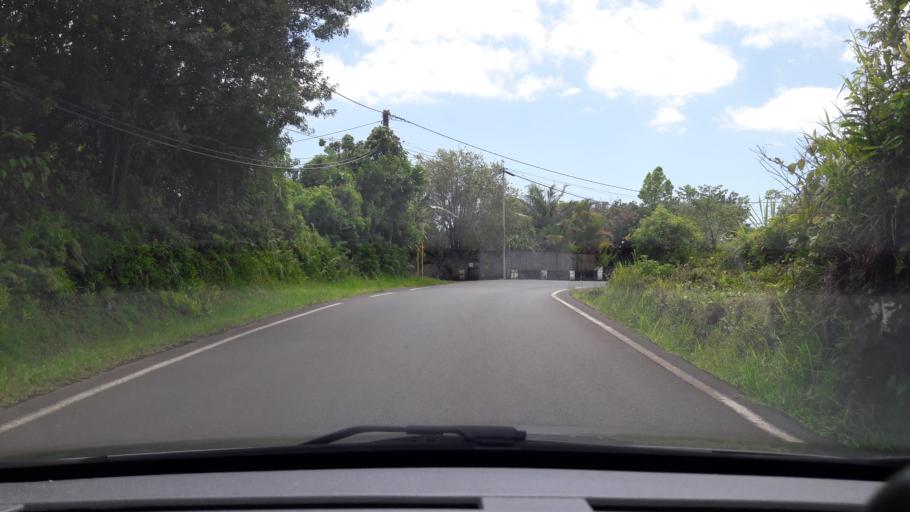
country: RE
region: Reunion
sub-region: Reunion
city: Saint-Benoit
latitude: -21.0920
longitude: 55.7037
